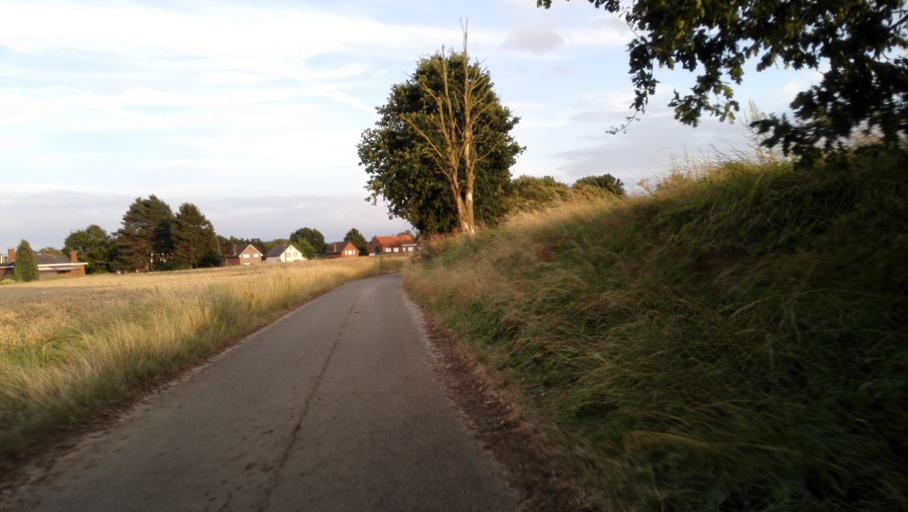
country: BE
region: Flanders
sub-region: Provincie Vlaams-Brabant
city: Bierbeek
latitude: 50.8364
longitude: 4.7448
